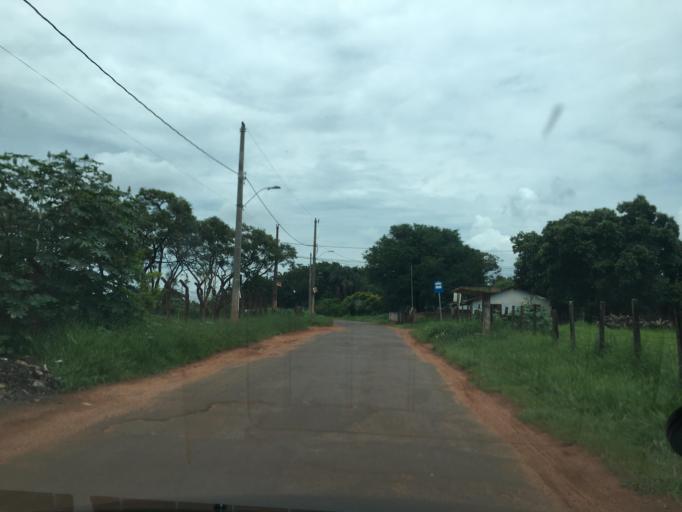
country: BR
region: Minas Gerais
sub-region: Uberlandia
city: Uberlandia
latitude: -18.8641
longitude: -48.2206
